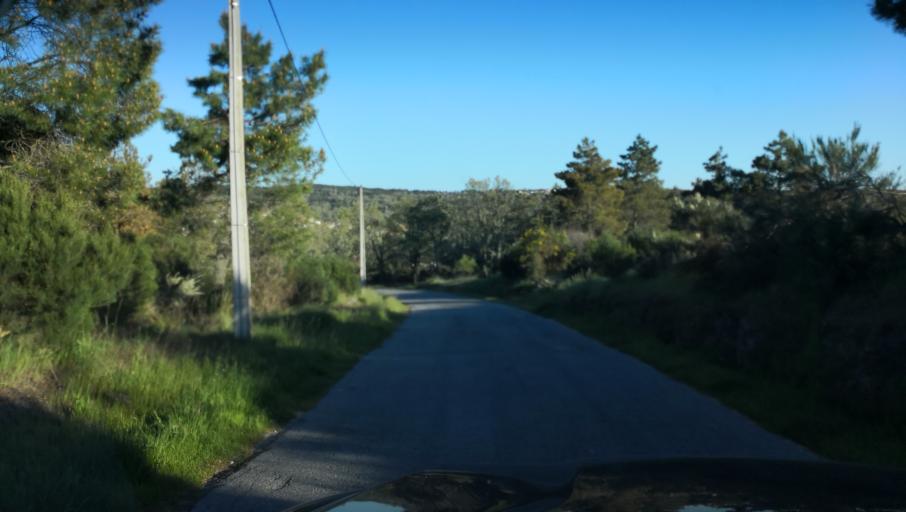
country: PT
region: Vila Real
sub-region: Vila Real
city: Vila Real
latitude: 41.3567
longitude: -7.6503
